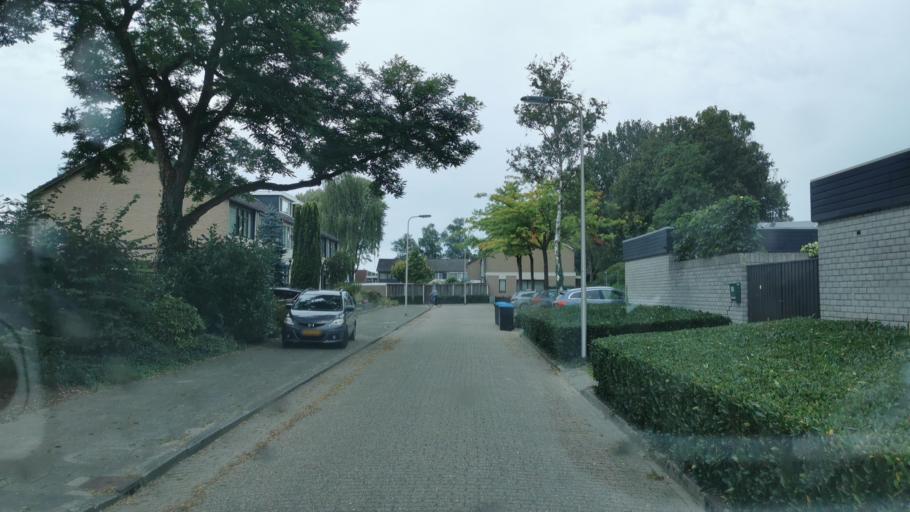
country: NL
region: Overijssel
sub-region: Gemeente Enschede
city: Enschede
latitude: 52.2301
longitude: 6.9183
